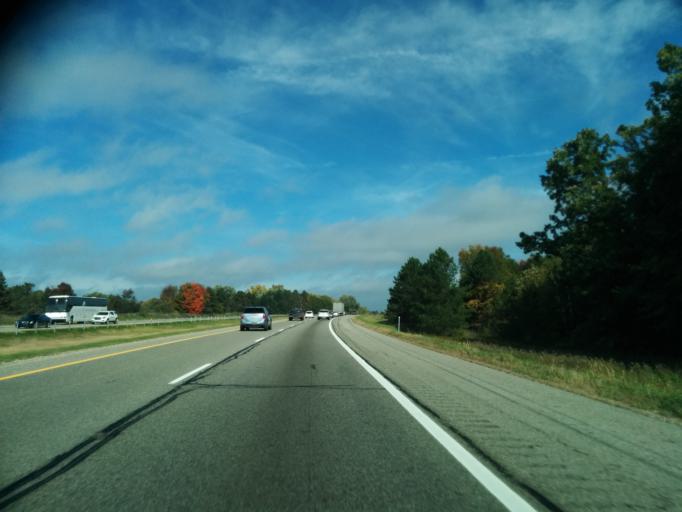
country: US
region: Michigan
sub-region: Livingston County
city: Brighton
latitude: 42.5933
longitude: -83.7403
